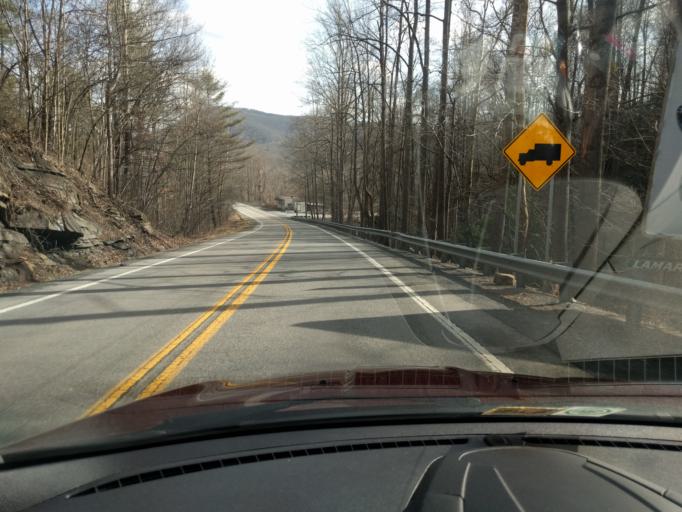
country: US
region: West Virginia
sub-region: Greenbrier County
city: Lewisburg
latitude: 37.7863
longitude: -80.4038
